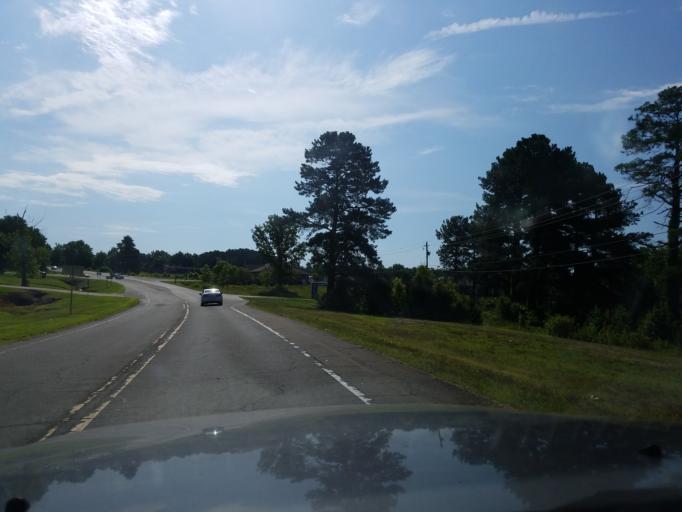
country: US
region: North Carolina
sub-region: Granville County
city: Oxford
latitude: 36.3130
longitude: -78.5554
